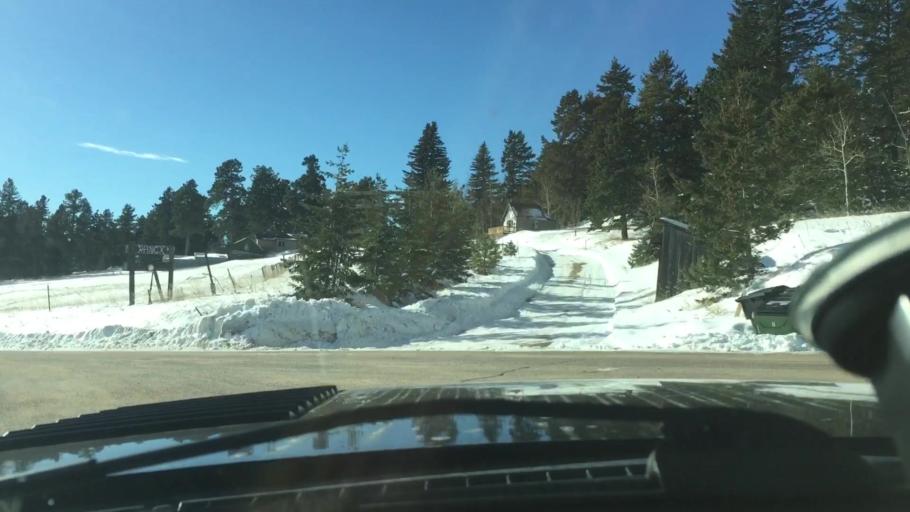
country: US
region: Colorado
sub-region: Jefferson County
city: Indian Hills
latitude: 39.5628
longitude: -105.2532
